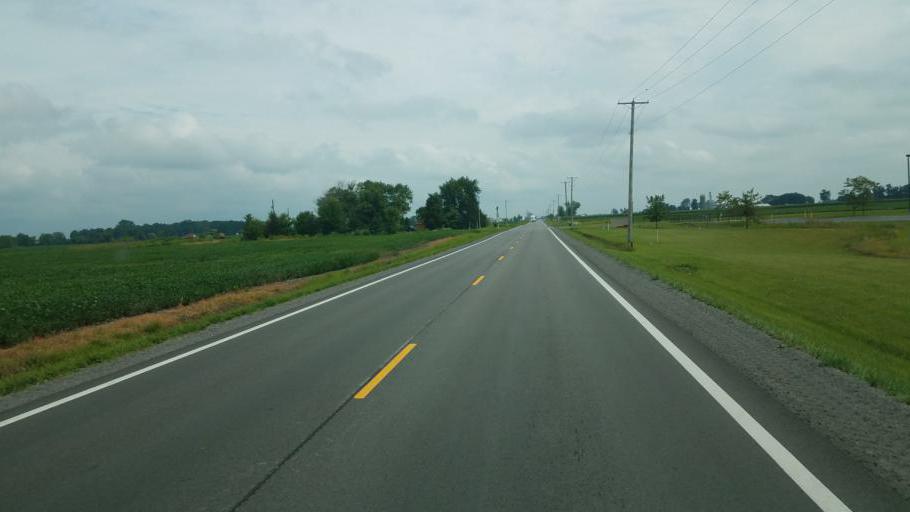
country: US
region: Ohio
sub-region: Marion County
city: Marion
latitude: 40.5716
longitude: -83.0434
